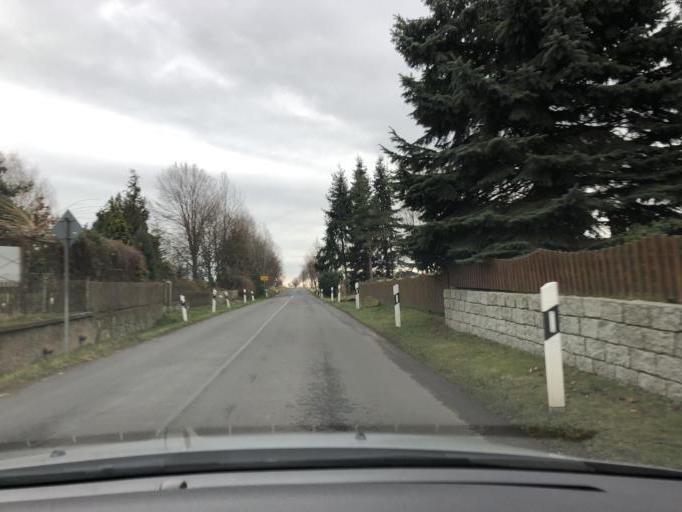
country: DE
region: Saxony
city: Nossen
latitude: 51.0737
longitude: 13.3007
